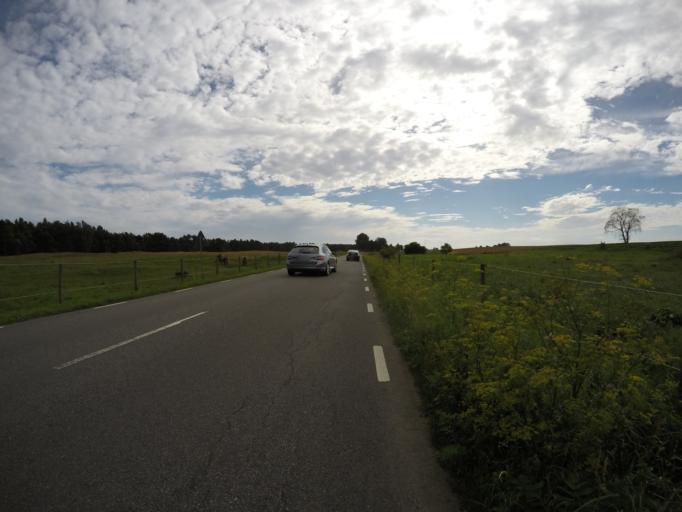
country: SE
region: Skane
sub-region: Simrishamns Kommun
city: Simrishamn
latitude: 55.4301
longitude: 14.2223
